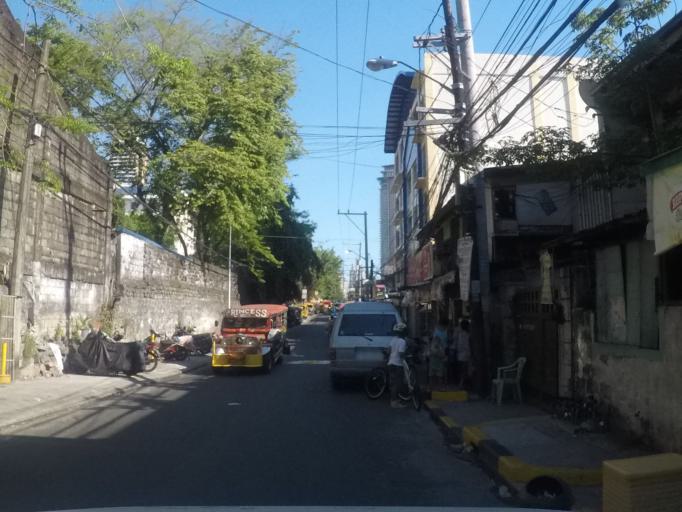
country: PH
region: Metro Manila
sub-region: San Juan
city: San Juan
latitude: 14.6086
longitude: 121.0505
